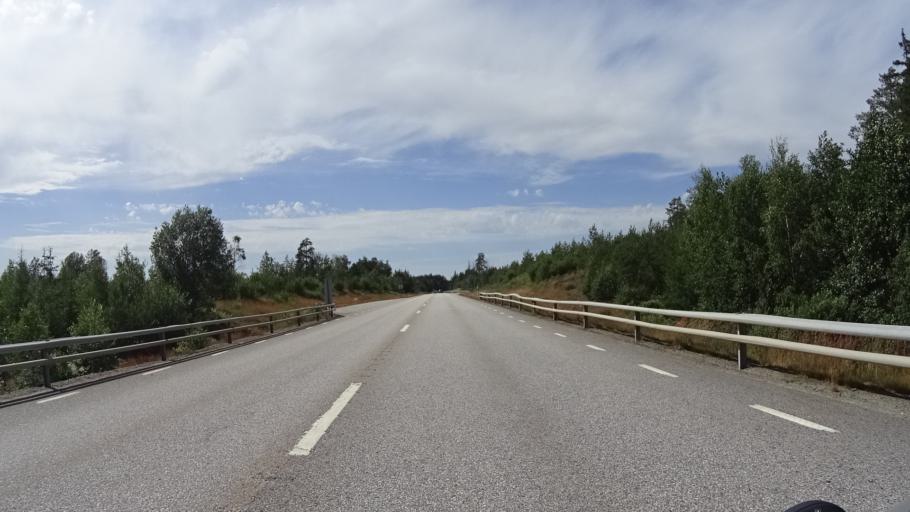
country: SE
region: Kalmar
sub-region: Vasterviks Kommun
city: Overum
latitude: 57.9612
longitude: 16.3600
